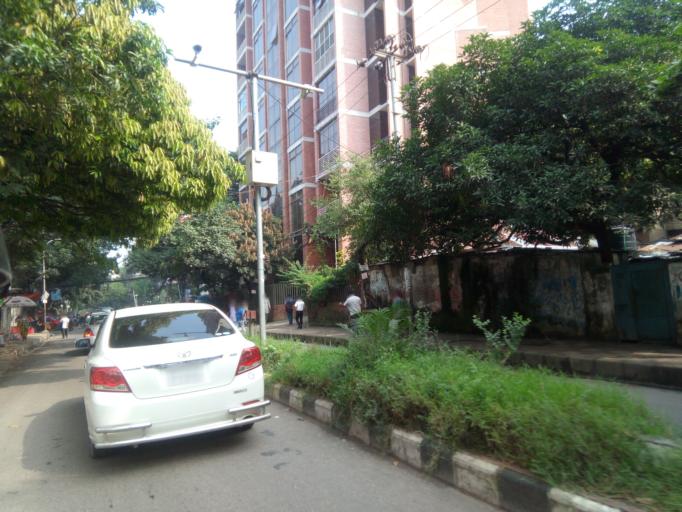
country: BD
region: Dhaka
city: Paltan
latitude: 23.7880
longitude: 90.4001
